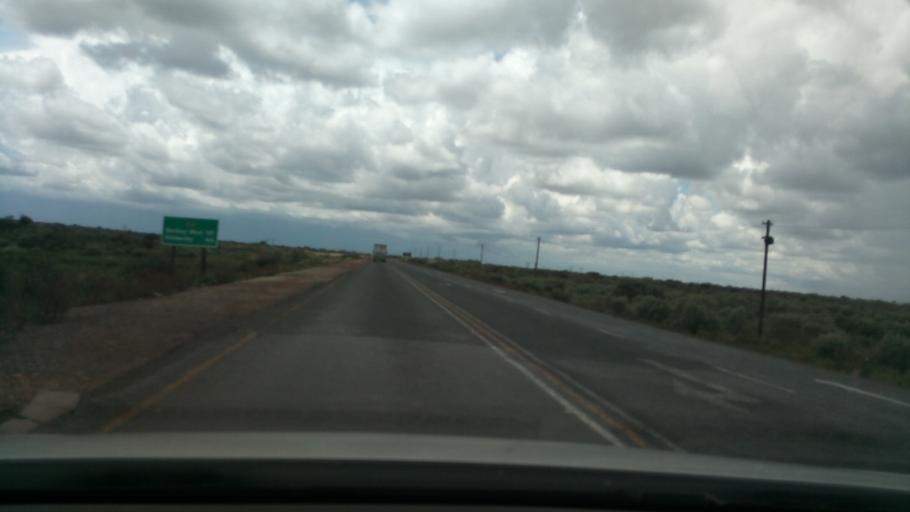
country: ZA
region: Northern Cape
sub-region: Siyanda District Municipality
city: Danielskuil
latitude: -28.2624
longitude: 23.5600
